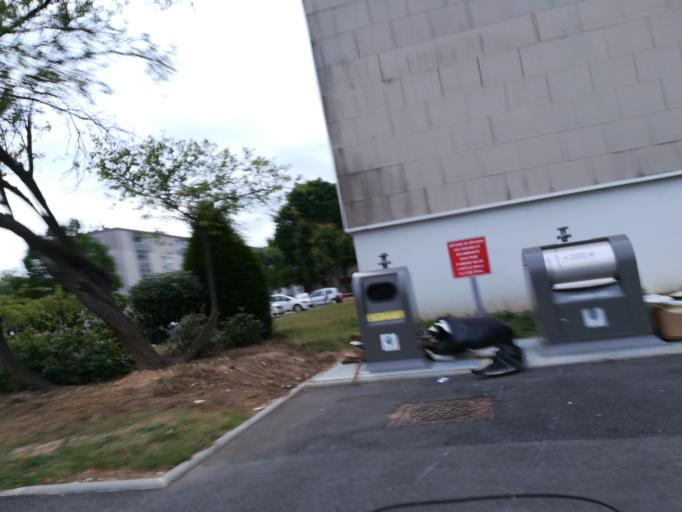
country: FR
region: Haute-Normandie
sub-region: Departement de la Seine-Maritime
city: Deville-les-Rouen
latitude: 49.4631
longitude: 1.0695
